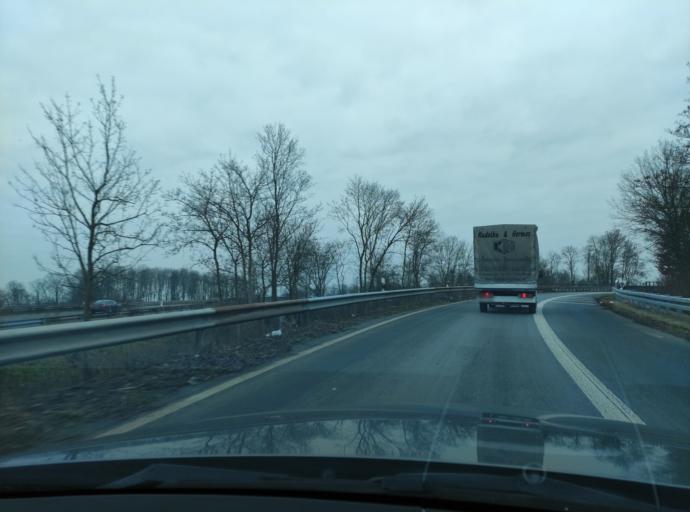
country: DE
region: North Rhine-Westphalia
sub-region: Regierungsbezirk Dusseldorf
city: Moers
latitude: 51.4395
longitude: 6.6701
